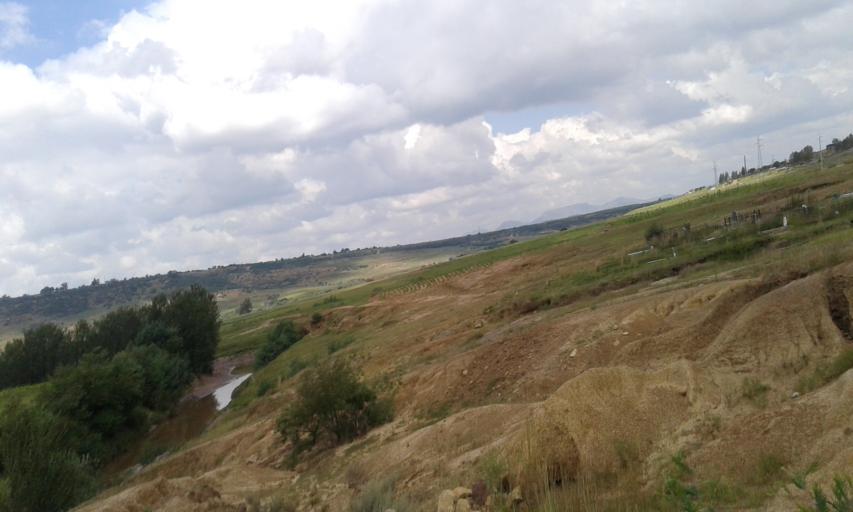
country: LS
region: Maseru
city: Maseru
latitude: -29.4148
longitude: 27.5703
